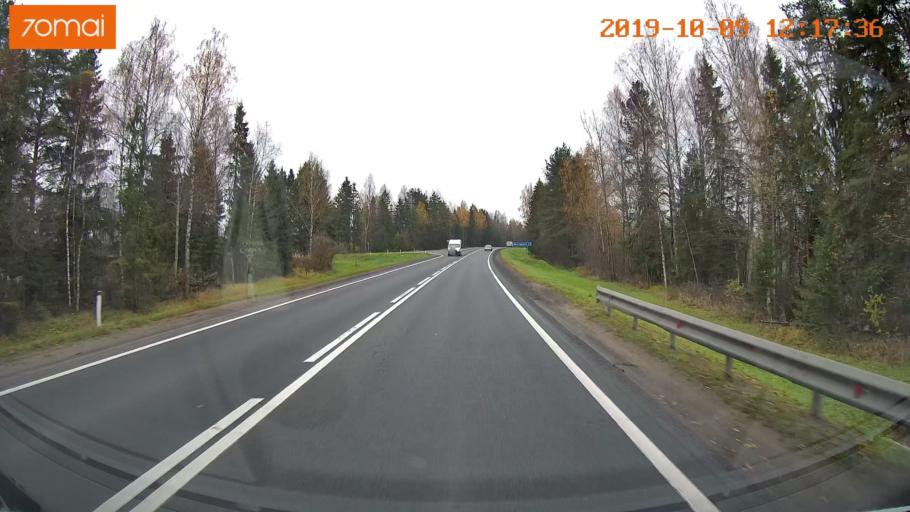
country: RU
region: Jaroslavl
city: Prechistoye
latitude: 58.4539
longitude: 40.3217
